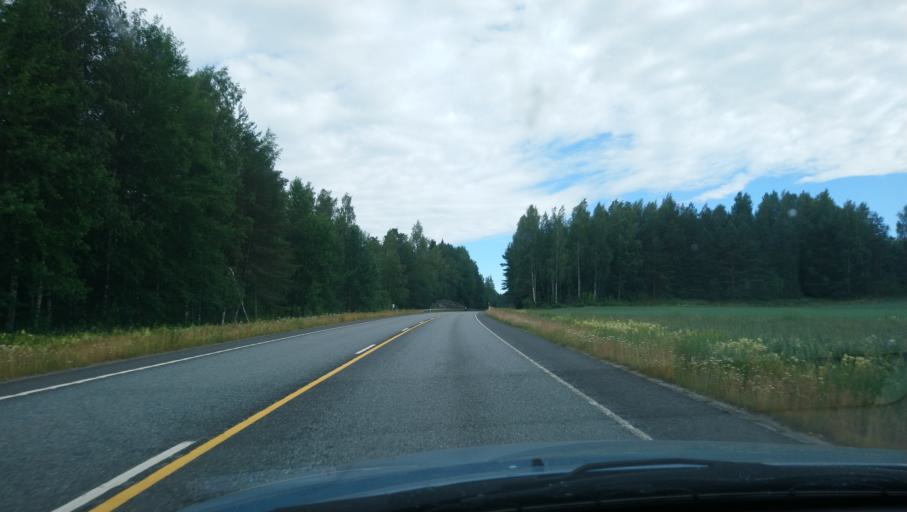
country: FI
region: Uusimaa
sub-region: Porvoo
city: Porvoo
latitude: 60.4175
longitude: 25.5795
